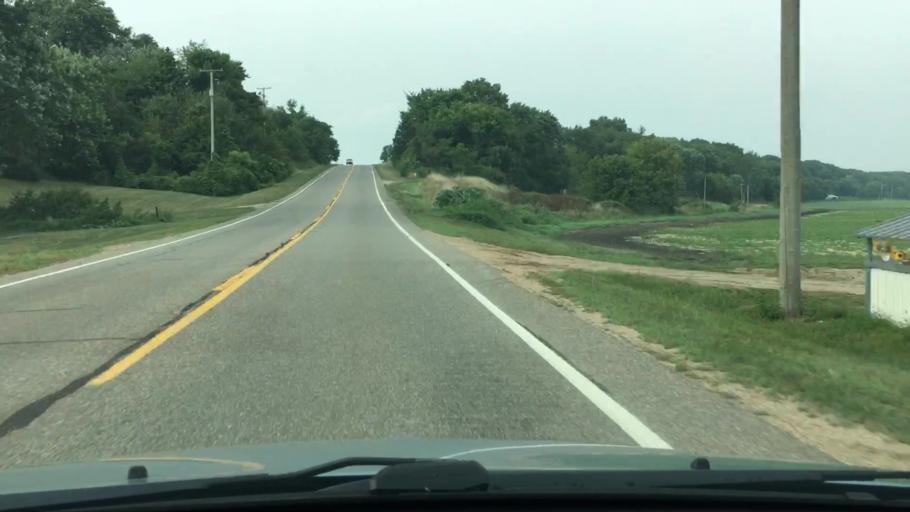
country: US
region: Michigan
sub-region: Ottawa County
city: Hudsonville
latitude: 42.8630
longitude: -85.9008
